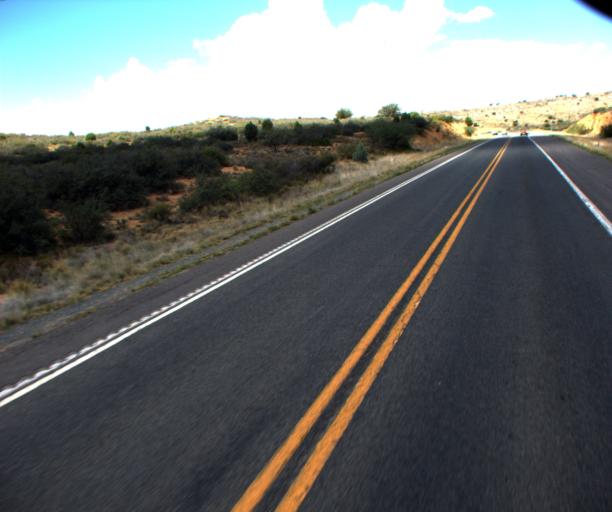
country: US
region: Arizona
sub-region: Yavapai County
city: Verde Village
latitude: 34.5225
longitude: -112.0427
